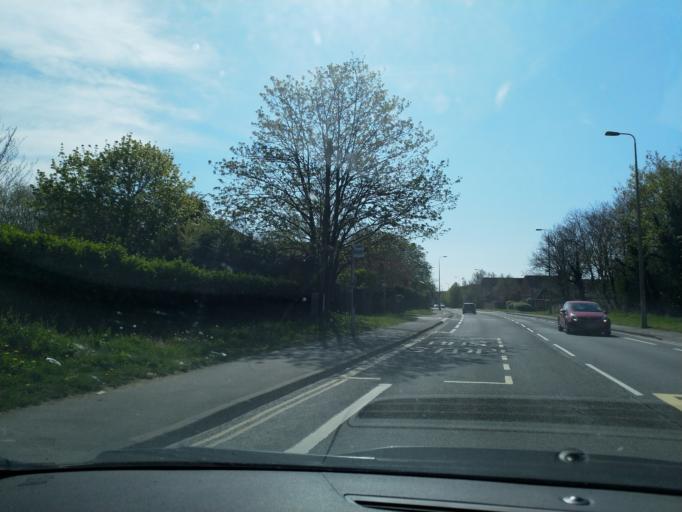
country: GB
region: England
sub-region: Oxfordshire
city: Cowley
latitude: 51.7438
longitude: -1.2003
